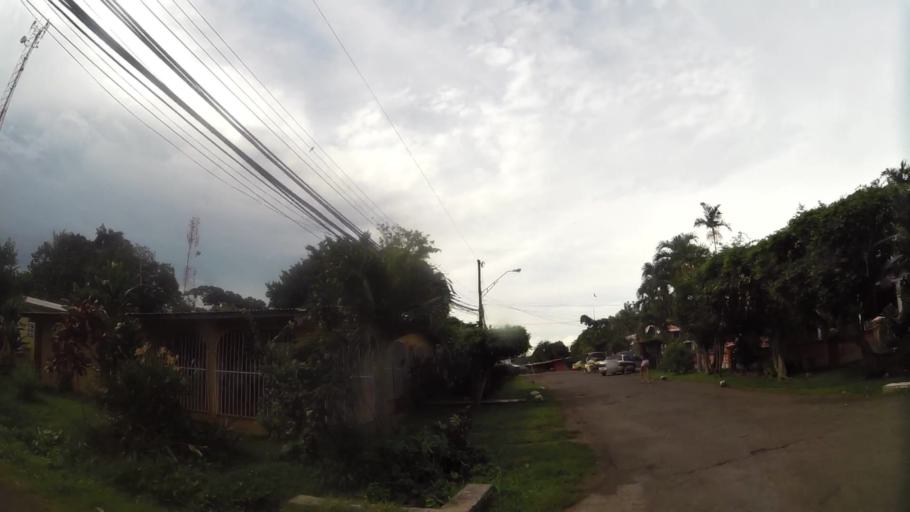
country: PA
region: Panama
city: El Coco
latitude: 8.8678
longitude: -79.8051
